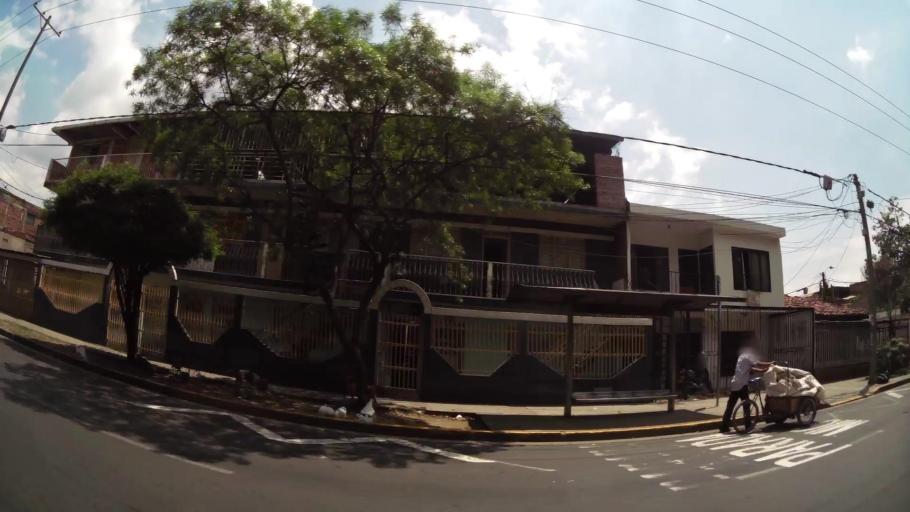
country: CO
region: Valle del Cauca
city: Cali
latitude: 3.4814
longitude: -76.4851
